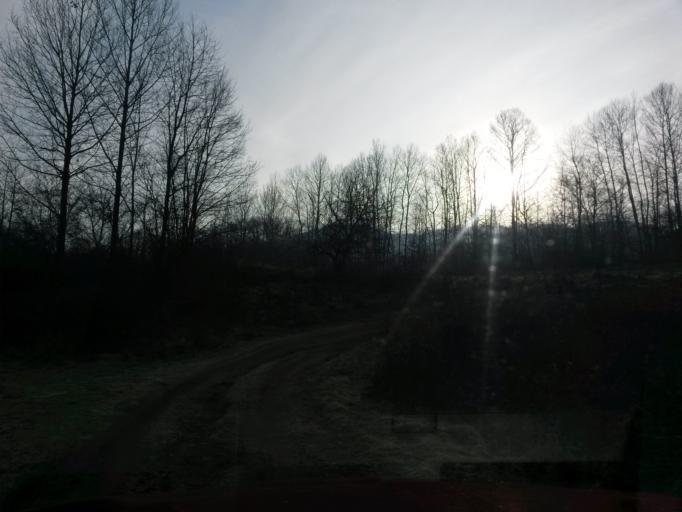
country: SK
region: Kosicky
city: Roznava
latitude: 48.7100
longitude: 20.4628
